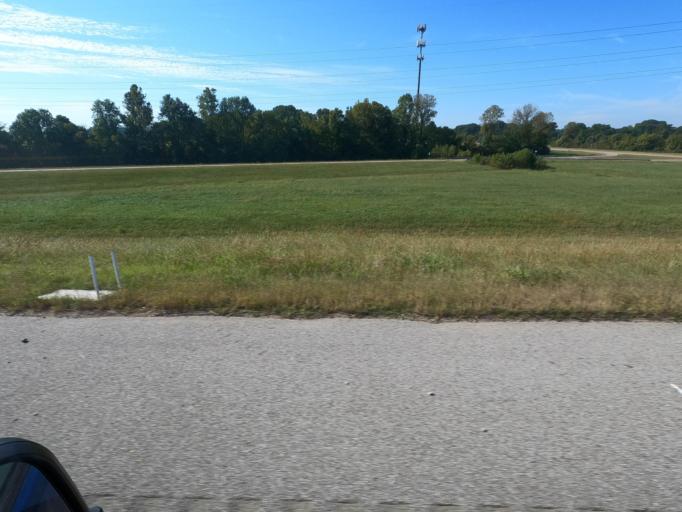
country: US
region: Tennessee
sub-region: Shelby County
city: Millington
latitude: 35.3182
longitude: -89.8717
